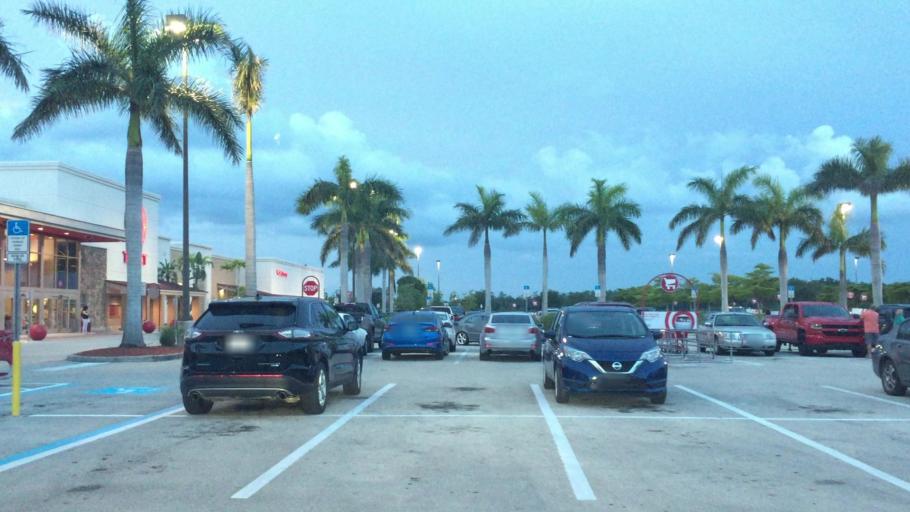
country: US
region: Florida
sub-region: Lee County
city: Fort Myers
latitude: 26.6147
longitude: -81.8010
